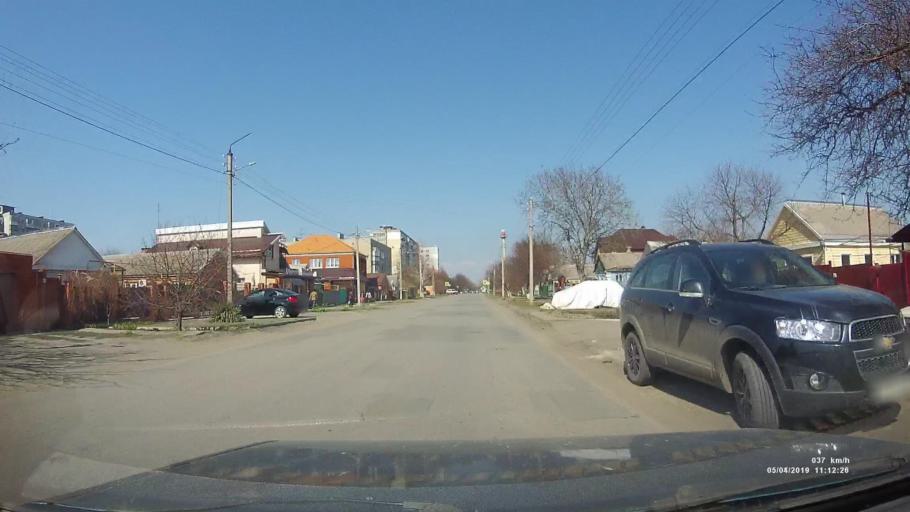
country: RU
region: Rostov
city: Azov
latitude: 47.0979
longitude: 39.4373
